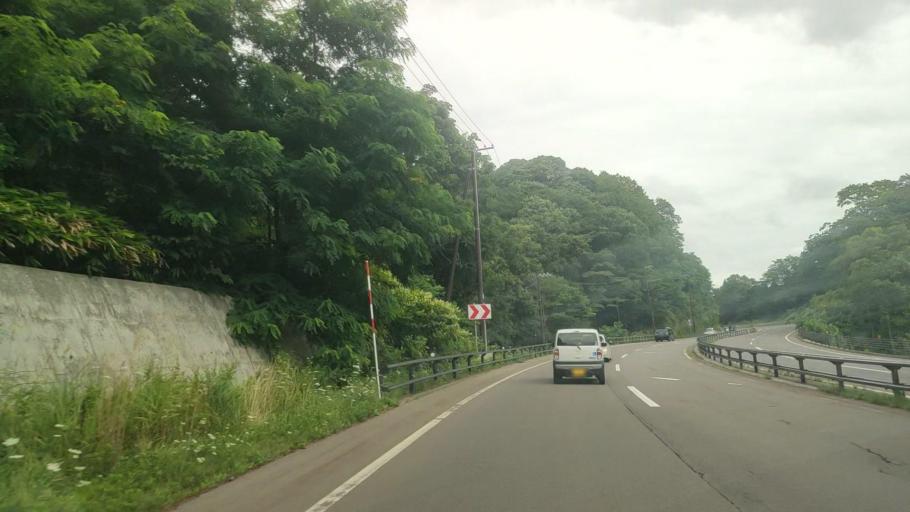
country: JP
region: Hokkaido
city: Nanae
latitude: 41.9631
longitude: 140.6476
